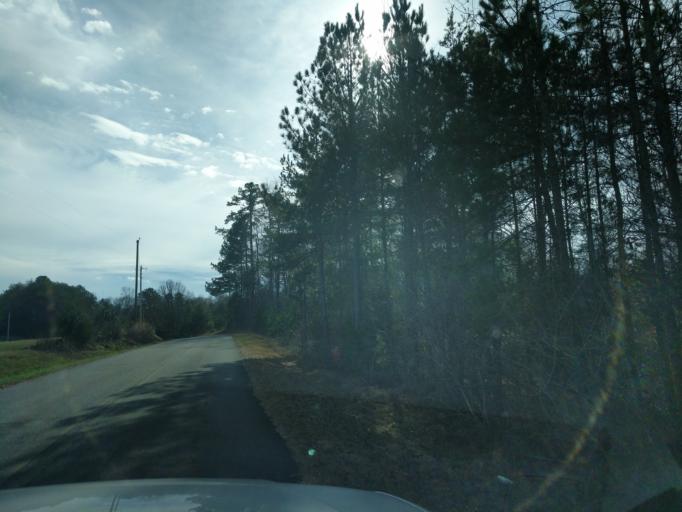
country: US
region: South Carolina
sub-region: Oconee County
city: Walhalla
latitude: 34.8576
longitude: -83.0545
